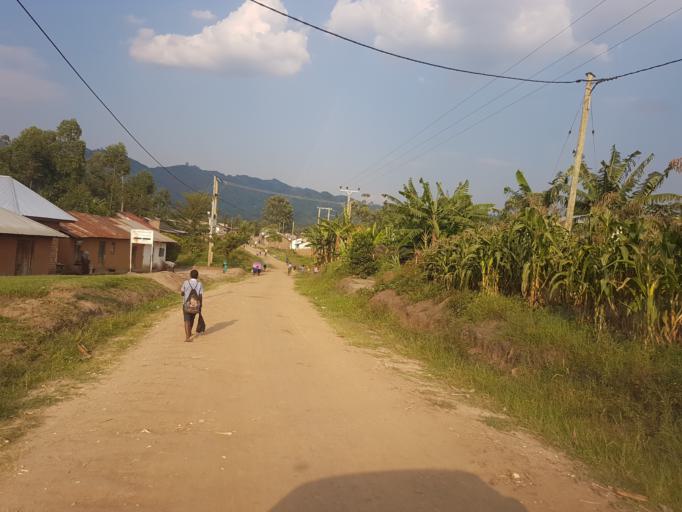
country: UG
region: Western Region
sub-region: Rukungiri District
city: Rukungiri
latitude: -0.6712
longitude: 29.8834
